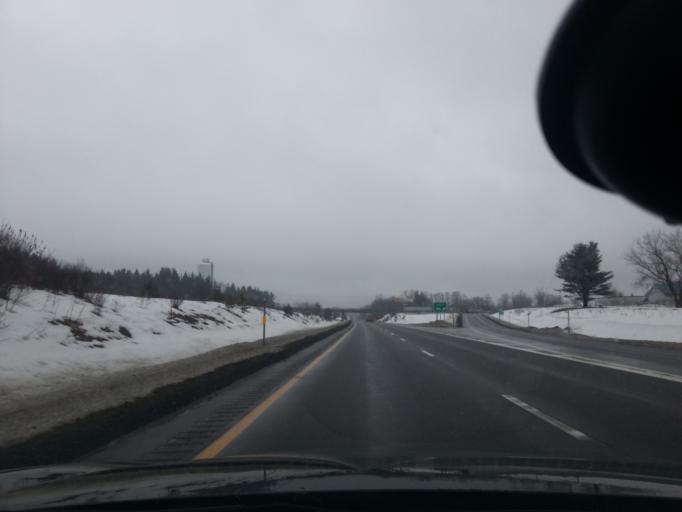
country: US
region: New York
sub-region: Oswego County
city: Pulaski
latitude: 43.5704
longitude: -76.1138
